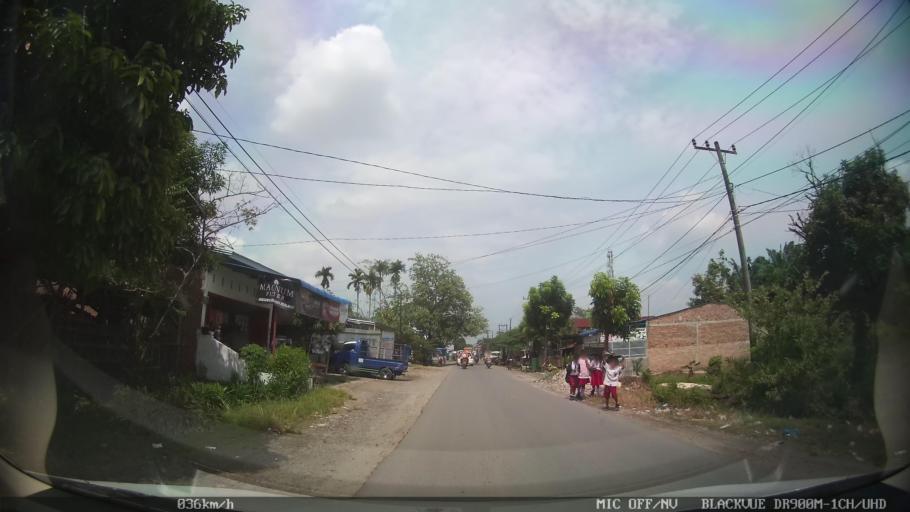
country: ID
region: North Sumatra
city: Medan
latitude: 3.6508
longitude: 98.7036
